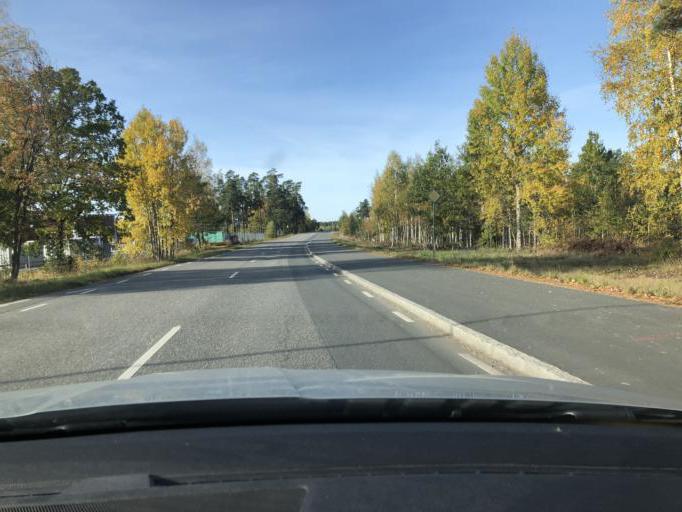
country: SE
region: Joenkoeping
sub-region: Jonkopings Kommun
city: Jonkoping
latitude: 57.7717
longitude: 14.0927
